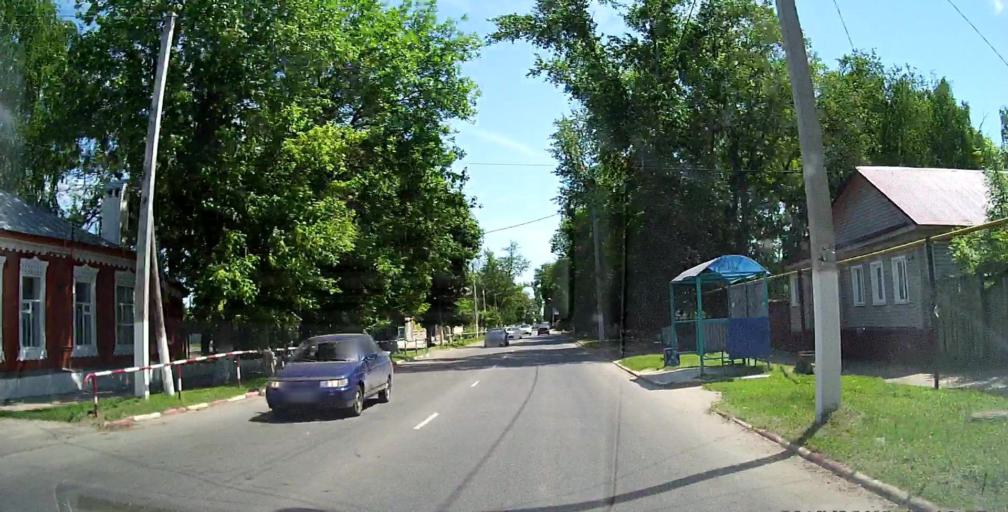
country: RU
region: Lipetsk
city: Chaplygin
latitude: 53.2422
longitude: 39.9662
